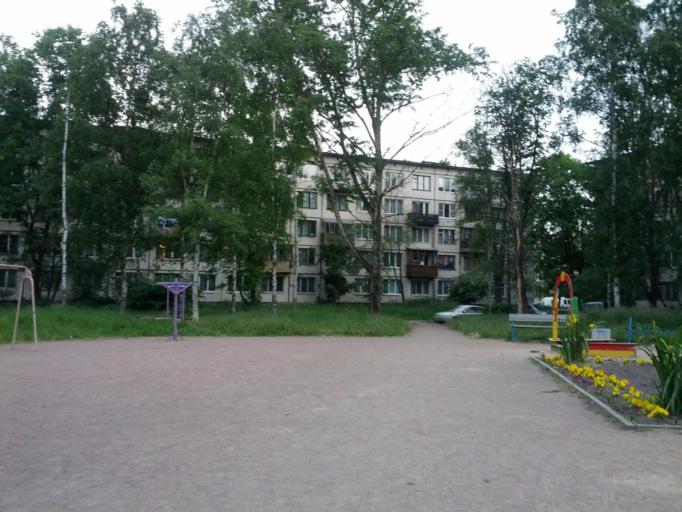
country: RU
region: St.-Petersburg
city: Obukhovo
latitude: 59.8935
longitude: 30.4751
